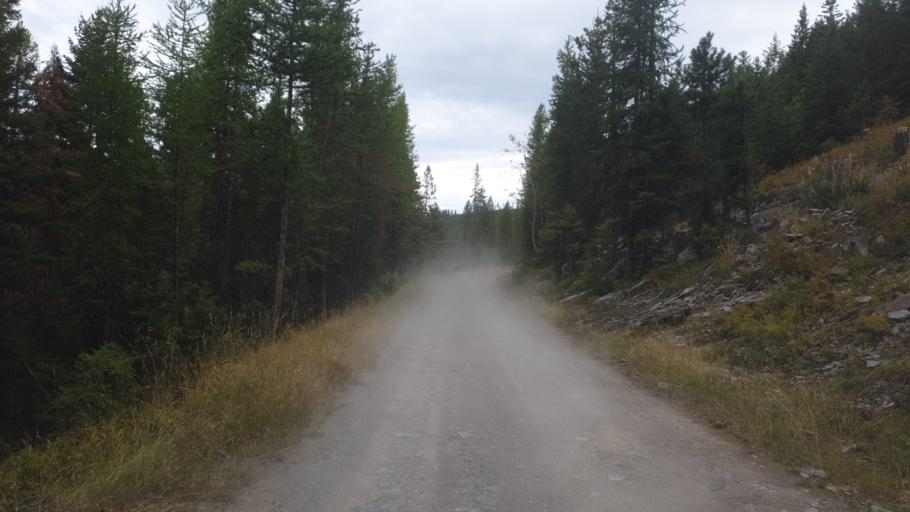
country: US
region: Montana
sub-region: Flathead County
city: Lakeside
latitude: 47.9884
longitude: -114.3229
